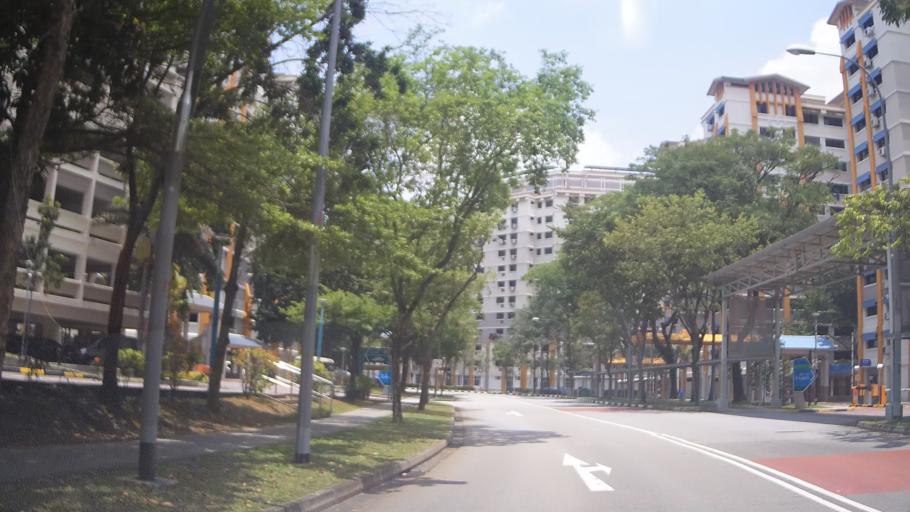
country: MY
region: Johor
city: Johor Bahru
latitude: 1.4430
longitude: 103.7994
